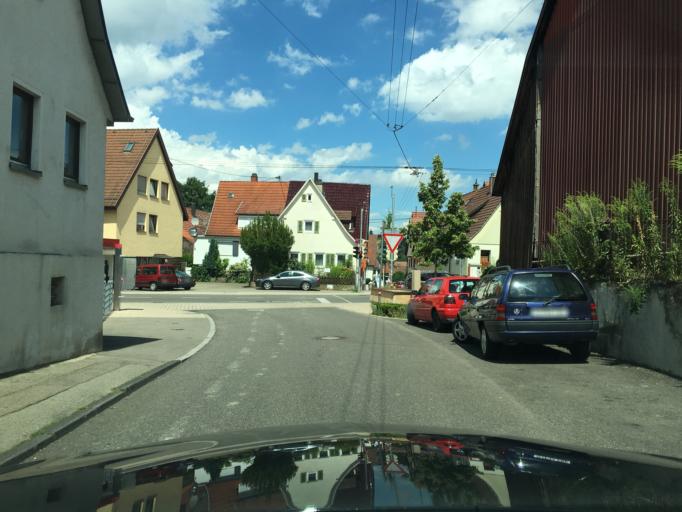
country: DE
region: Baden-Wuerttemberg
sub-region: Regierungsbezirk Stuttgart
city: Leinfelden-Echterdingen
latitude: 48.7008
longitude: 9.2110
